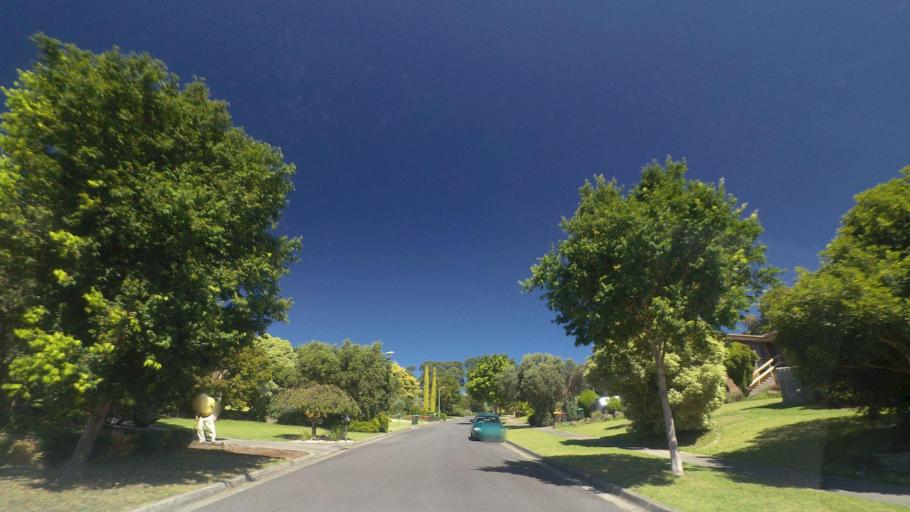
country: AU
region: Victoria
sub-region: Manningham
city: Donvale
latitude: -37.7682
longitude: 145.1791
